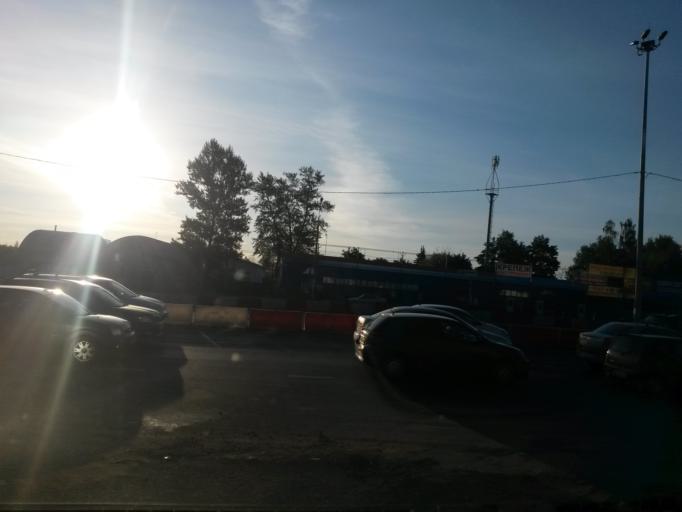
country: RU
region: Moskovskaya
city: Bolshevo
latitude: 55.9437
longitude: 37.8130
